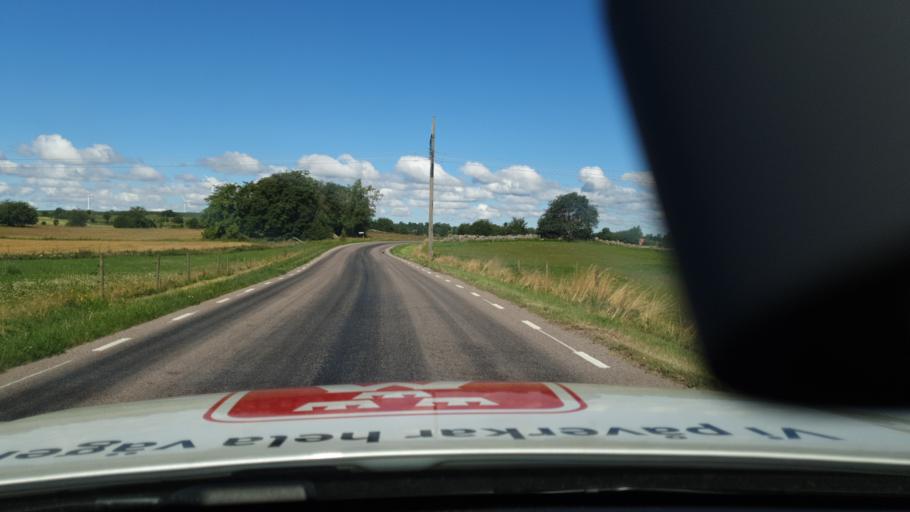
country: SE
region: Vaestra Goetaland
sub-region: Falkopings Kommun
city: Falkoeping
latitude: 58.2164
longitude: 13.5808
